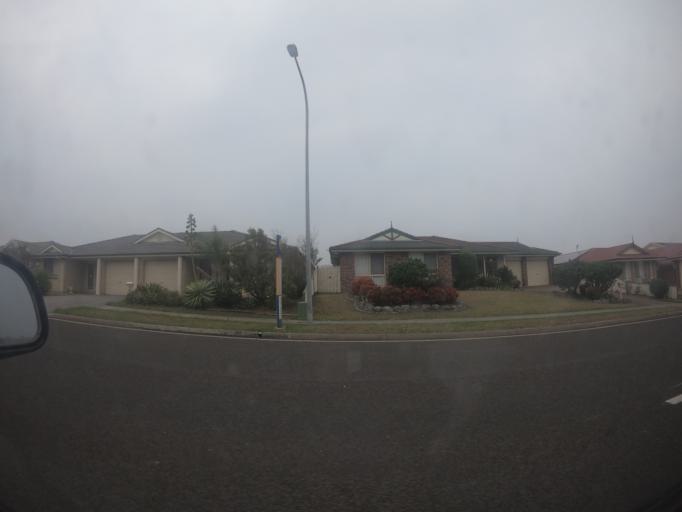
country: AU
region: New South Wales
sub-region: Shellharbour
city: Flinders
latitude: -34.5804
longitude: 150.8461
